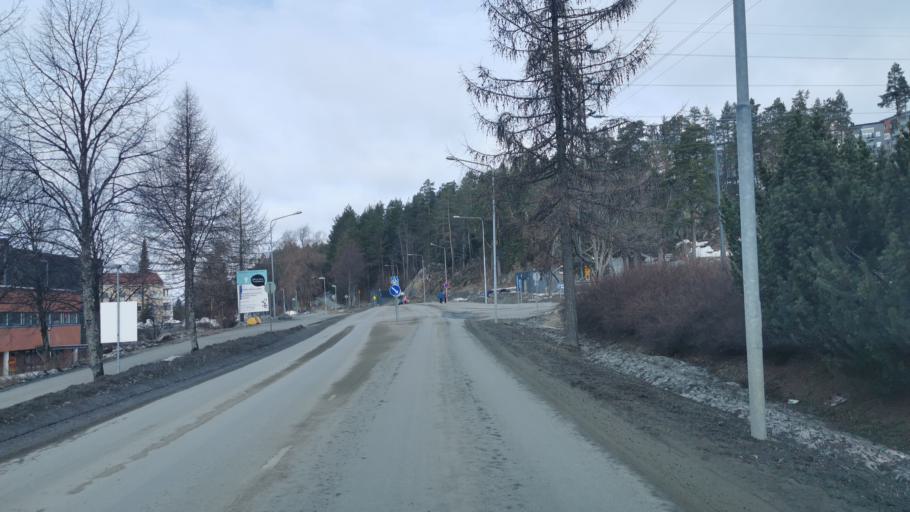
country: FI
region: Northern Savo
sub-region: Kuopio
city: Kuopio
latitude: 62.8966
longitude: 27.6427
